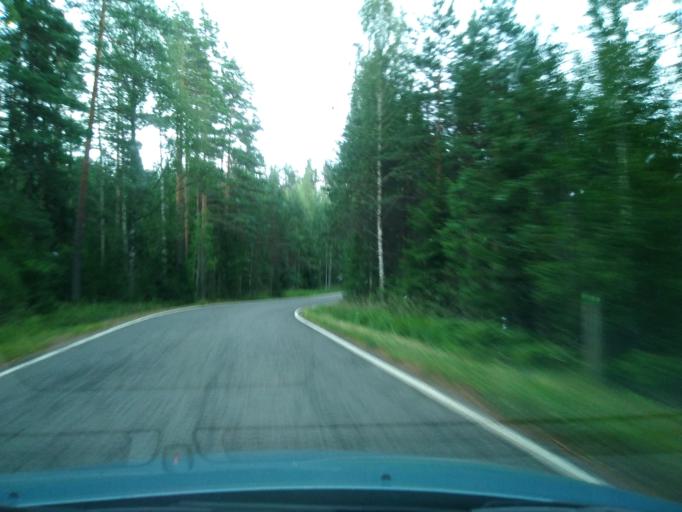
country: FI
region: Uusimaa
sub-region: Helsinki
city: Kaerkoelae
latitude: 60.7865
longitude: 24.0803
